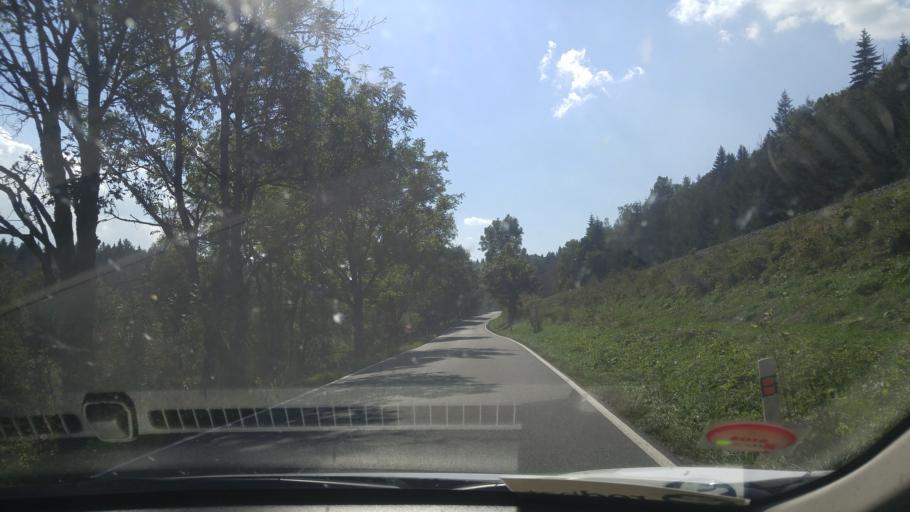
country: CZ
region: Olomoucky
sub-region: Okres Sumperk
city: Stare Mesto
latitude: 50.1703
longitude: 17.0307
